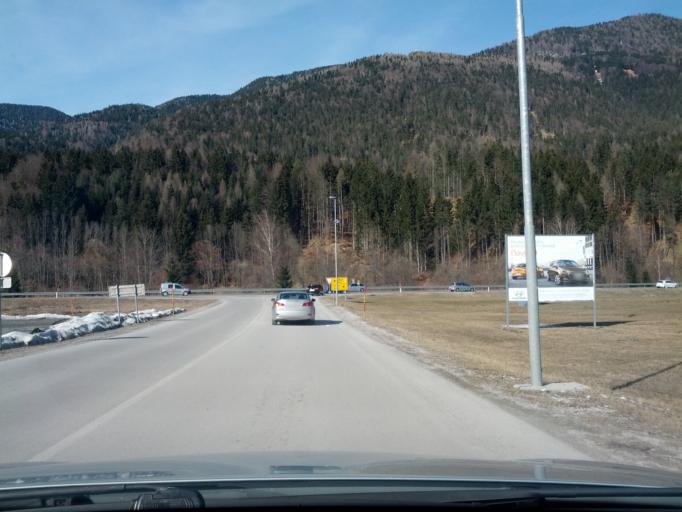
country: SI
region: Kranjska Gora
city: Kranjska Gora
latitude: 46.4872
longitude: 13.7790
